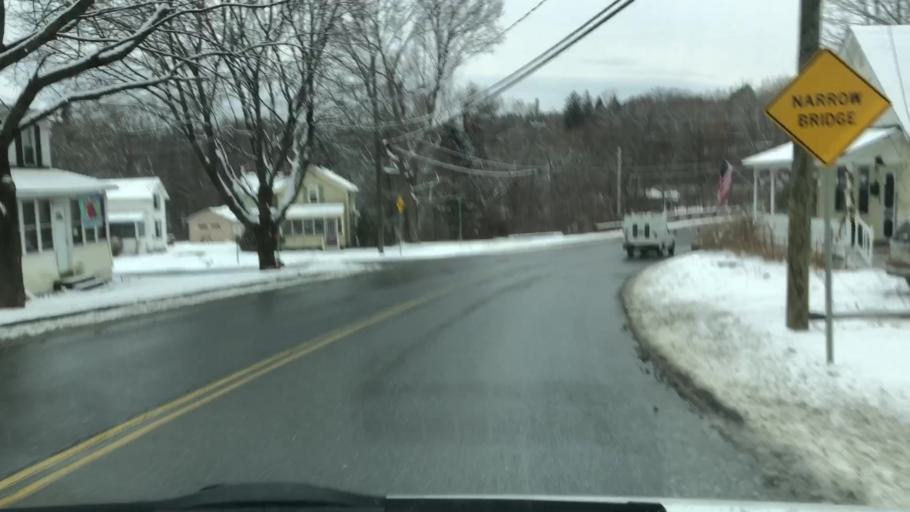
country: US
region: Massachusetts
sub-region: Berkshire County
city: Dalton
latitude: 42.4678
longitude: -73.1821
